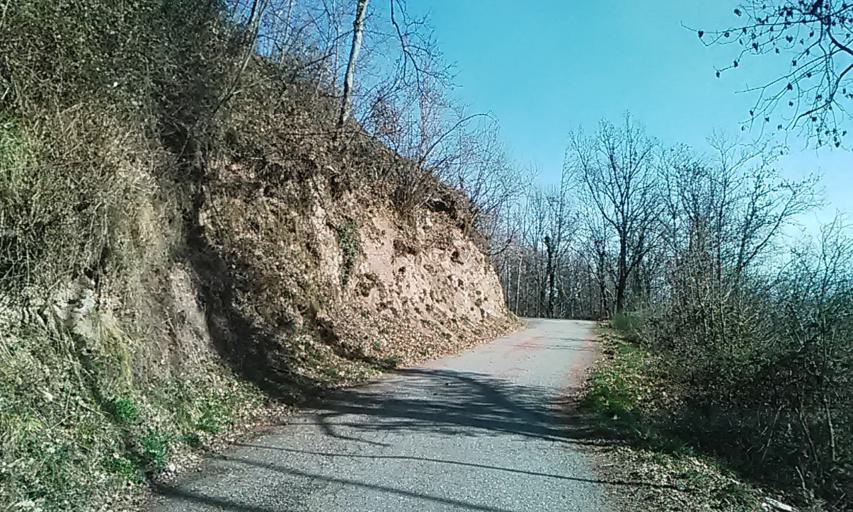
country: IT
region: Piedmont
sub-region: Provincia di Biella
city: Curino
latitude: 45.6495
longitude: 8.2455
